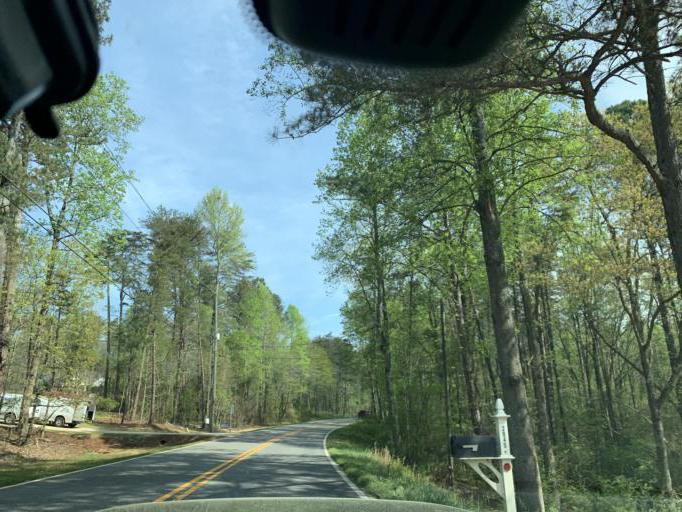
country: US
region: Georgia
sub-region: Forsyth County
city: Cumming
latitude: 34.2222
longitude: -84.0845
